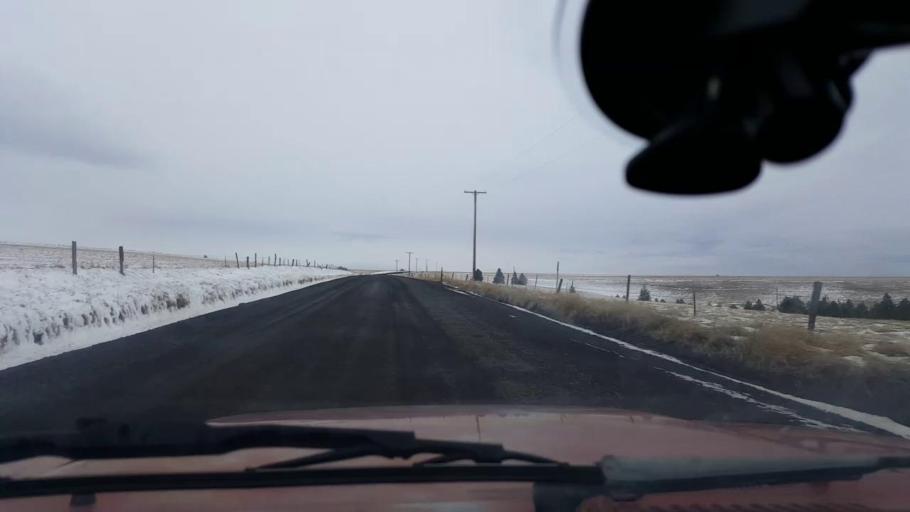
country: US
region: Washington
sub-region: Garfield County
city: Pomeroy
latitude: 46.3195
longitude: -117.4006
